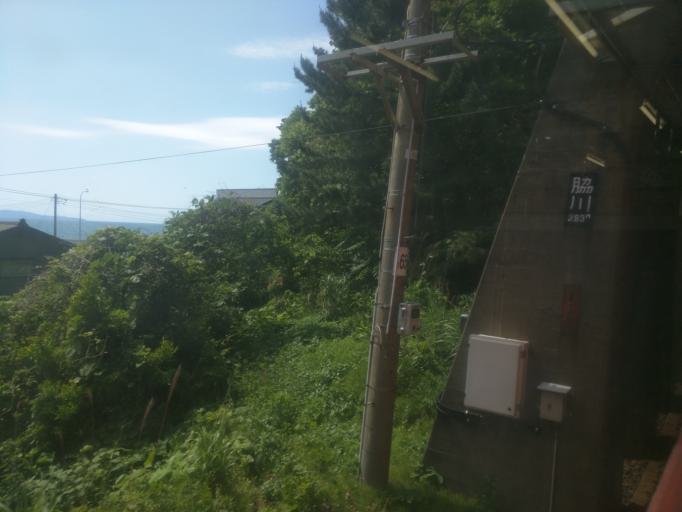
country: JP
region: Niigata
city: Murakami
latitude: 38.4377
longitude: 139.4835
